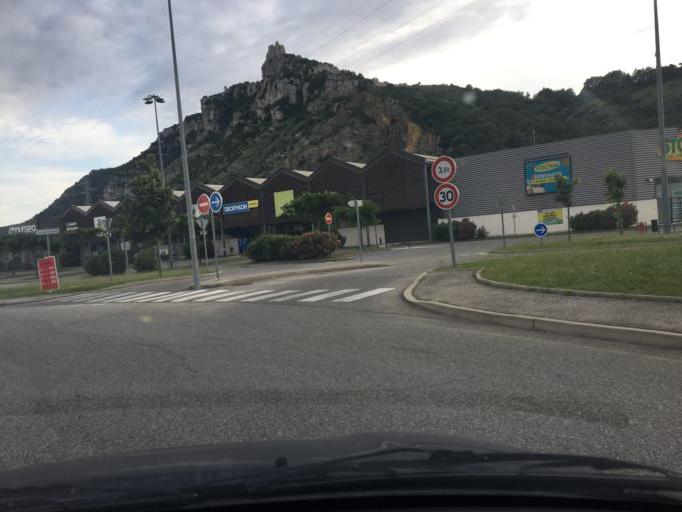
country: FR
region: Rhone-Alpes
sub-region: Departement de l'Ardeche
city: Saint-Peray
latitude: 44.9436
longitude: 4.8576
